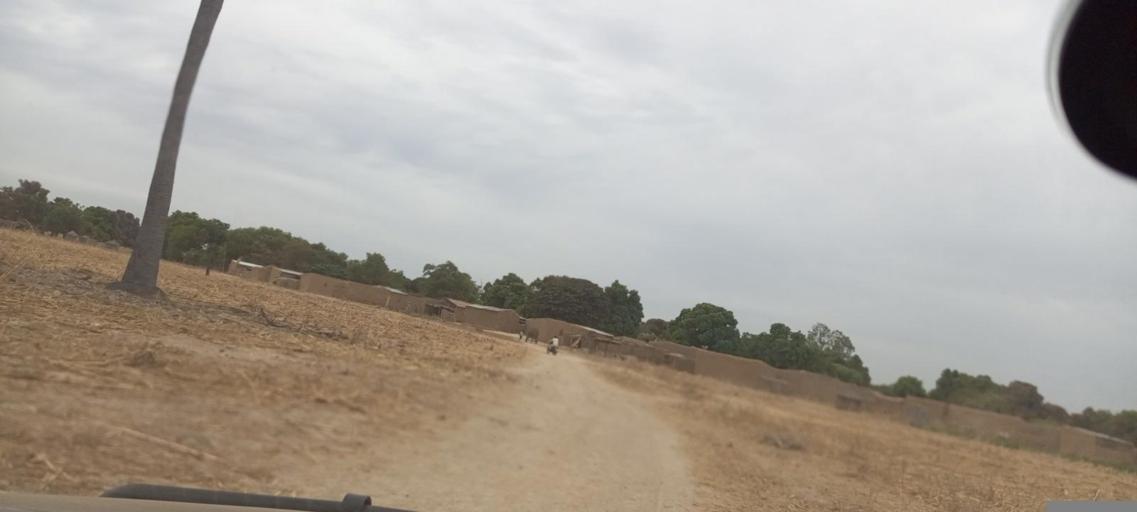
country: ML
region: Koulikoro
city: Kati
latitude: 12.7401
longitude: -8.3285
